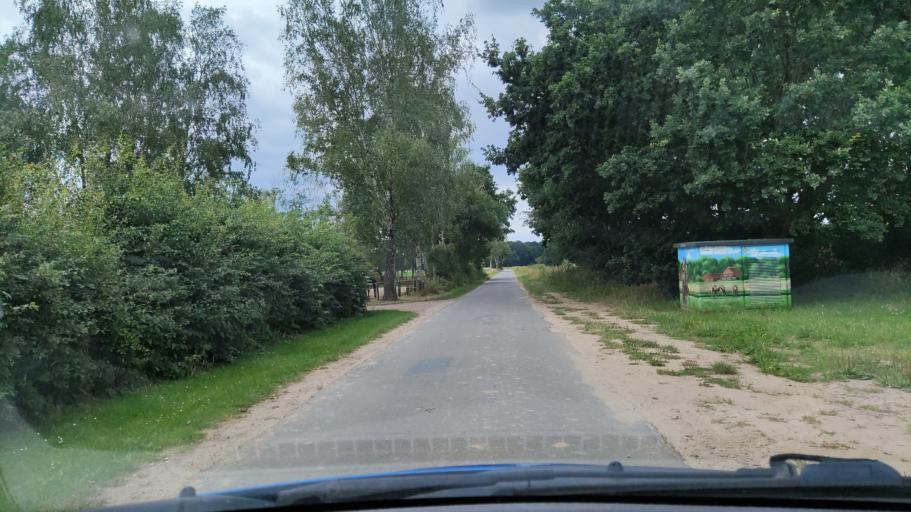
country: DE
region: Lower Saxony
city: Romstedt
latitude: 53.1057
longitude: 10.6779
